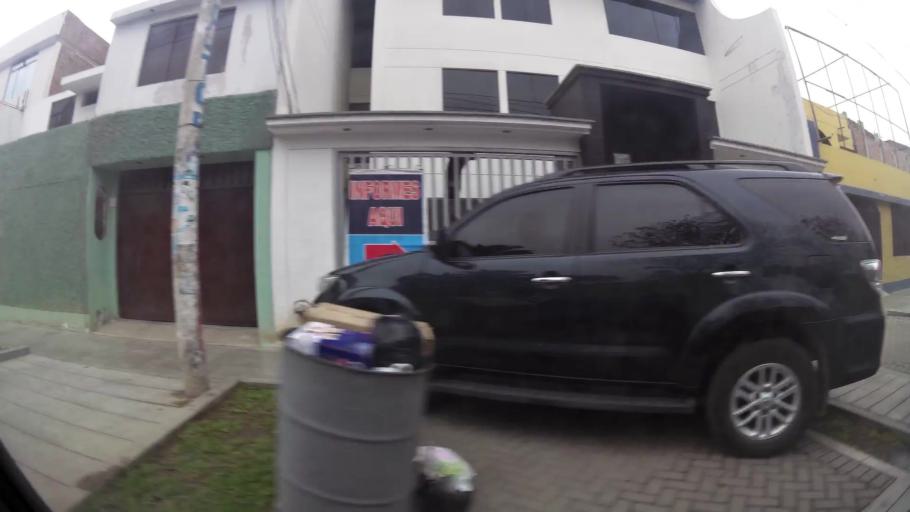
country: PE
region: La Libertad
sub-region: Provincia de Trujillo
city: Trujillo
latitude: -8.1085
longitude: -79.0372
